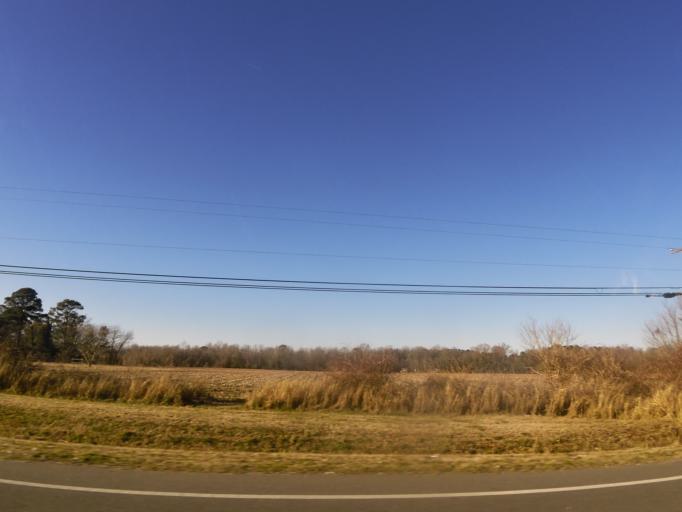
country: US
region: Virginia
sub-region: City of Franklin
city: Franklin
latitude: 36.6748
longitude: -76.7849
